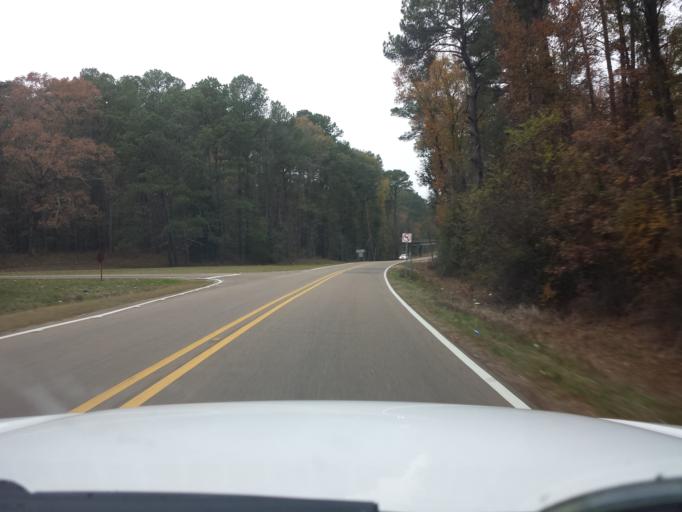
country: US
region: Mississippi
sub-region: Madison County
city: Canton
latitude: 32.5231
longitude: -89.9730
